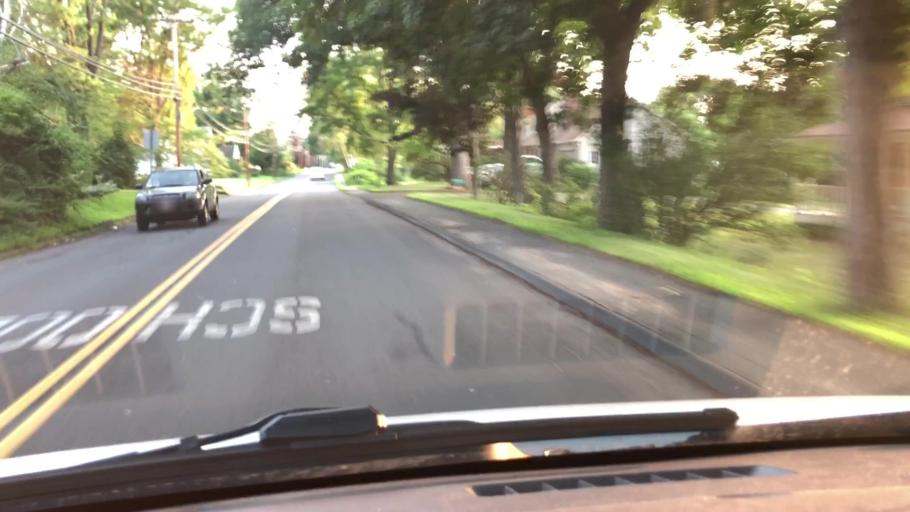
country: US
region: Massachusetts
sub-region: Hampshire County
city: Easthampton
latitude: 42.2535
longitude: -72.6789
